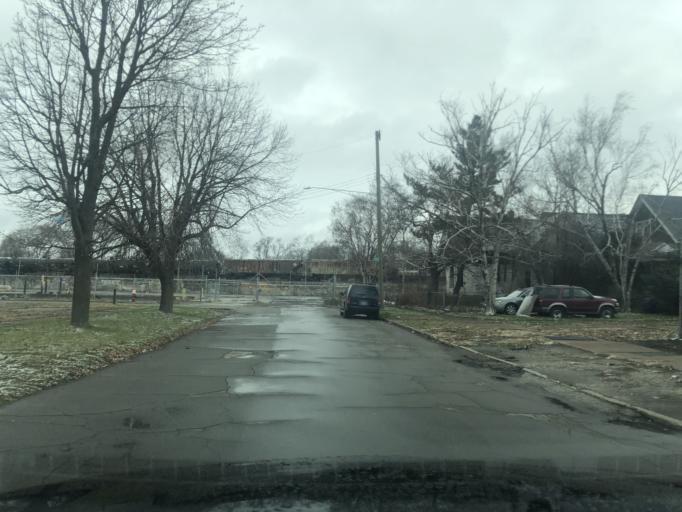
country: US
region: Michigan
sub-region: Wayne County
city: River Rouge
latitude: 42.3234
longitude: -83.1116
